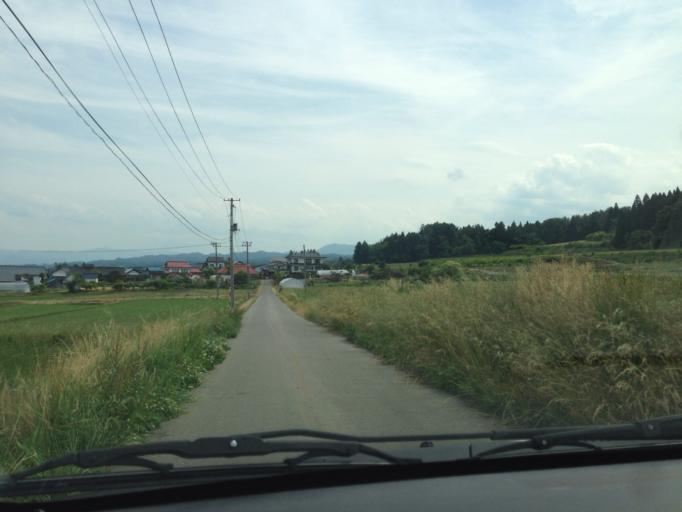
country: JP
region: Fukushima
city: Kitakata
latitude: 37.5567
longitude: 139.8001
